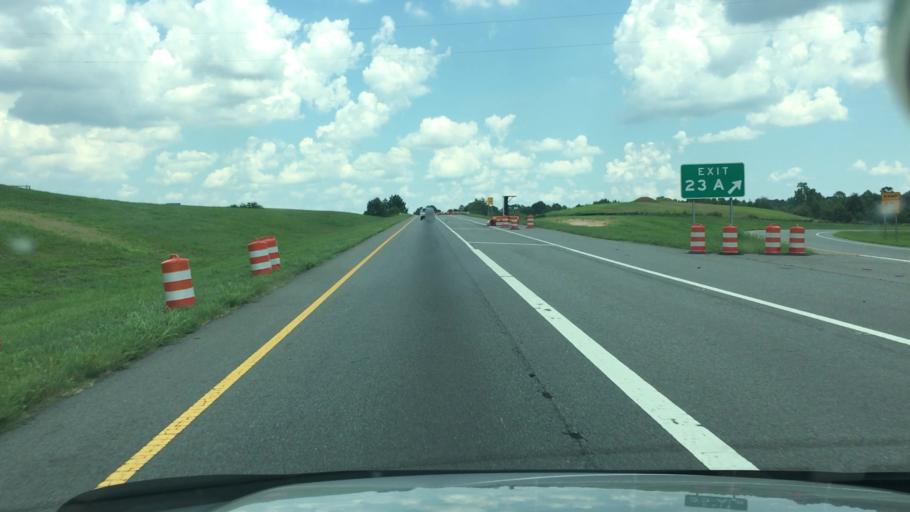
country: US
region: North Carolina
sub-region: Mecklenburg County
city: Huntersville
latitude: 35.3625
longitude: -80.8461
